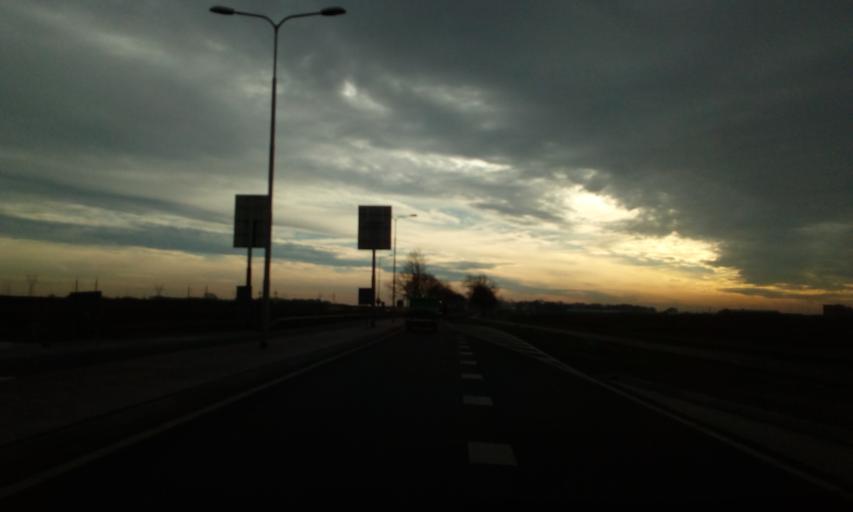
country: NL
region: South Holland
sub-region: Gemeente Rijnwoude
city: Benthuizen
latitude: 52.0730
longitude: 4.5590
